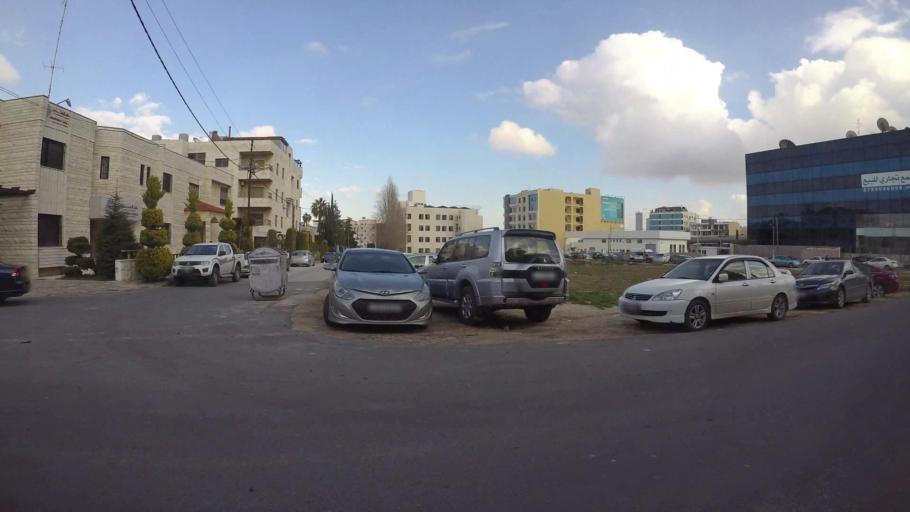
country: JO
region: Amman
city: Wadi as Sir
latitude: 31.9779
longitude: 35.8527
